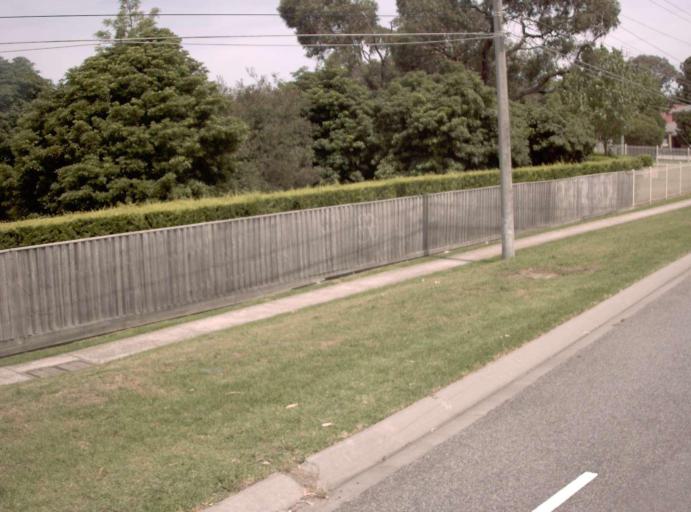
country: AU
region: Victoria
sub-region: Frankston
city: Frankston South
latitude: -38.1755
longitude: 145.1392
